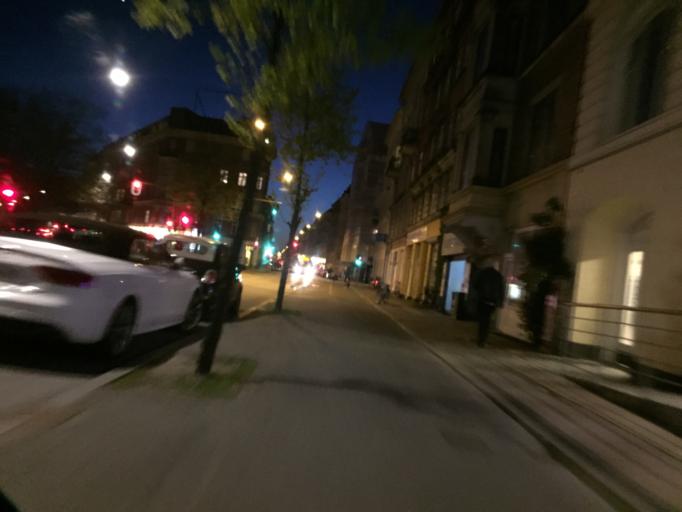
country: DK
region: Capital Region
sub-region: Kobenhavn
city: Copenhagen
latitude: 55.6848
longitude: 12.5542
